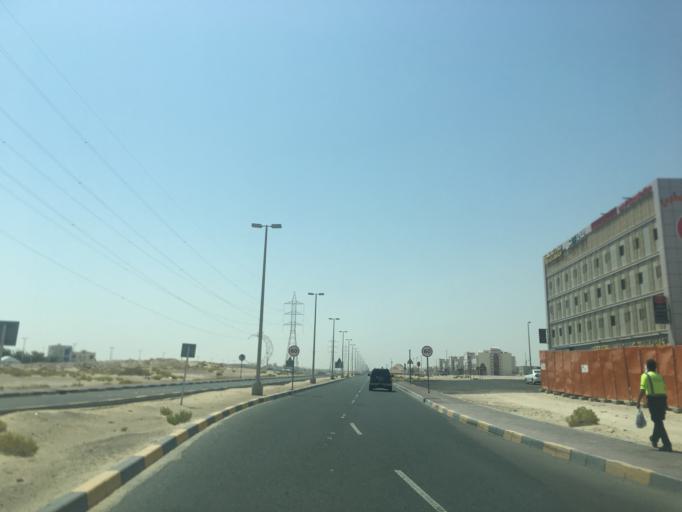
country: AE
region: Abu Dhabi
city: Abu Dhabi
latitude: 24.3186
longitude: 54.6312
